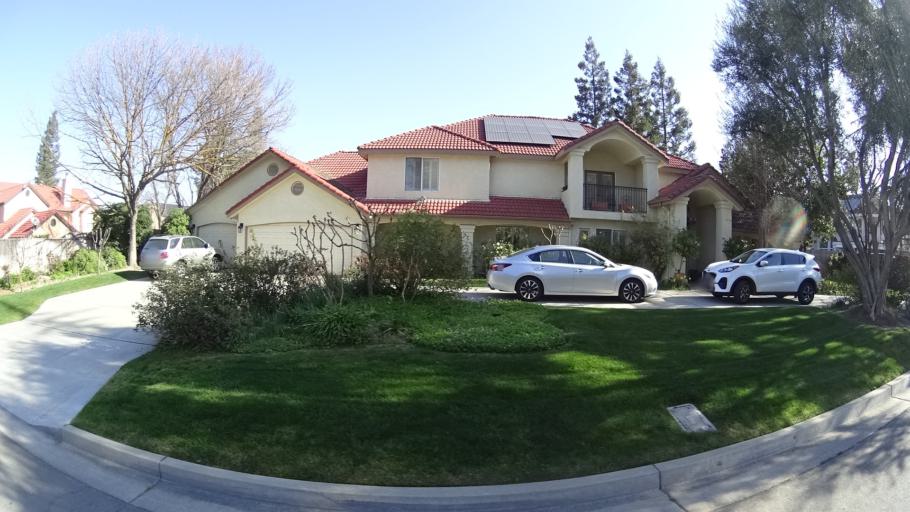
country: US
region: California
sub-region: Fresno County
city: Clovis
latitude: 36.8558
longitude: -119.8004
